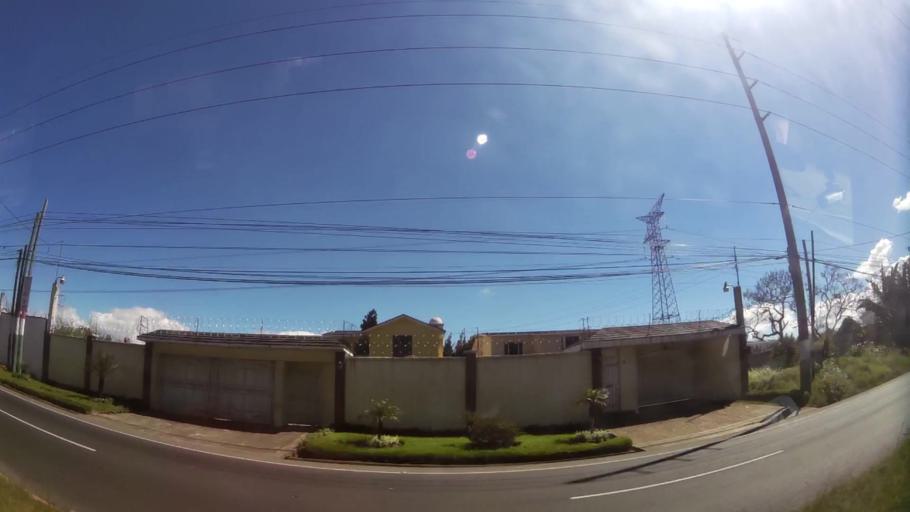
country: GT
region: Guatemala
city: Santa Catarina Pinula
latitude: 14.5211
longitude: -90.4706
